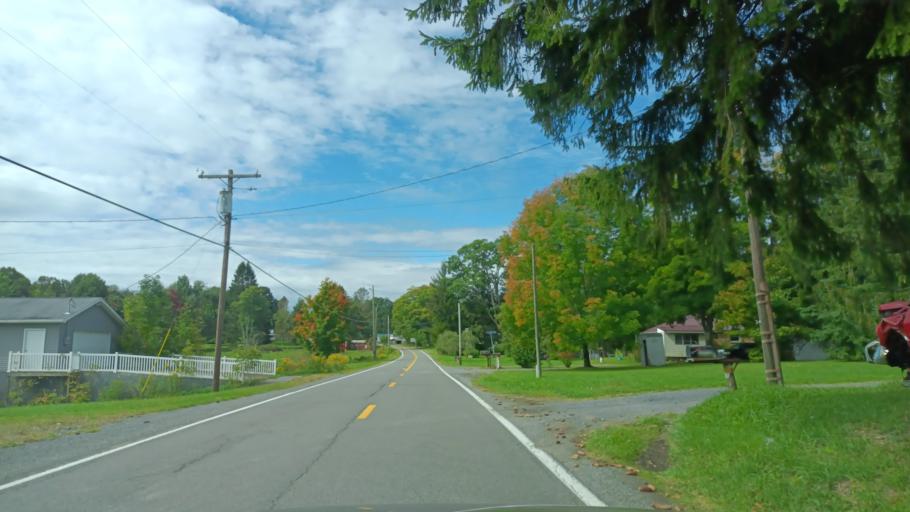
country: US
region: West Virginia
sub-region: Preston County
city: Terra Alta
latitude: 39.3147
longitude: -79.5824
